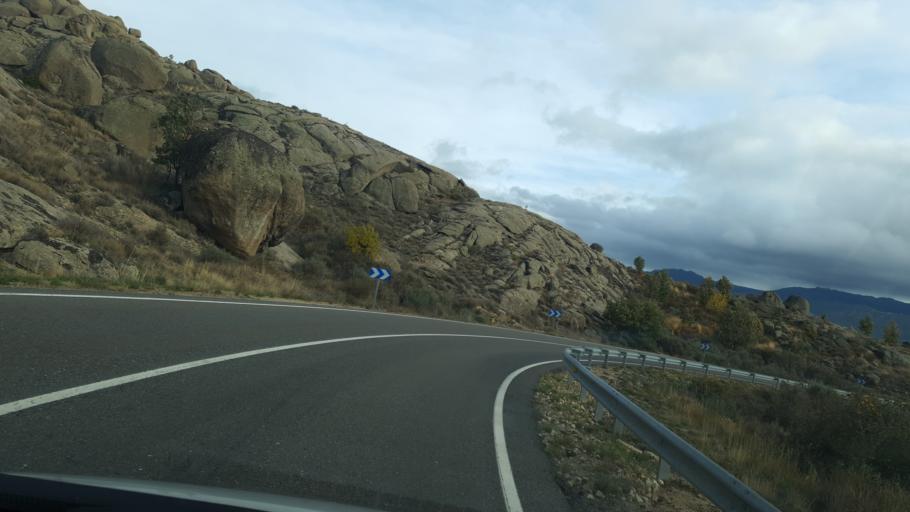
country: ES
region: Castille and Leon
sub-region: Provincia de Avila
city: Navalosa
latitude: 40.3959
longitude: -4.9169
